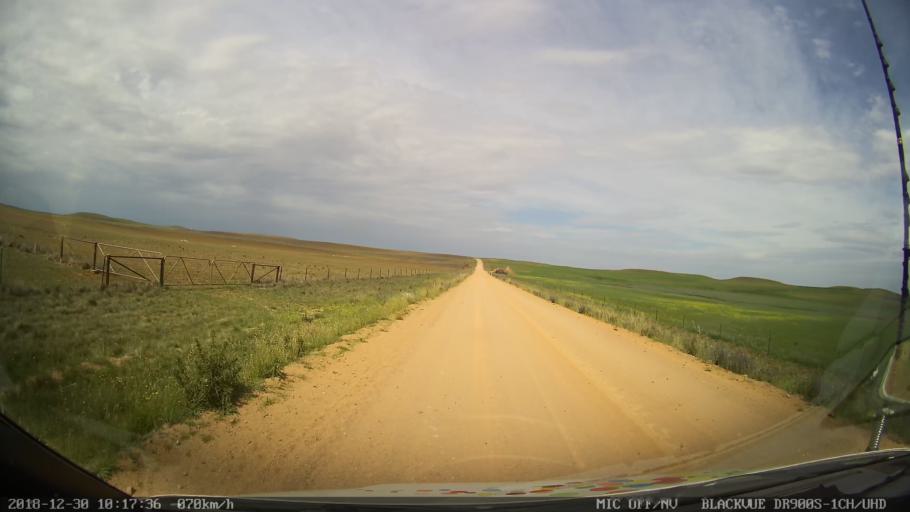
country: AU
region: New South Wales
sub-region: Snowy River
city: Berridale
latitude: -36.5491
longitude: 149.0190
